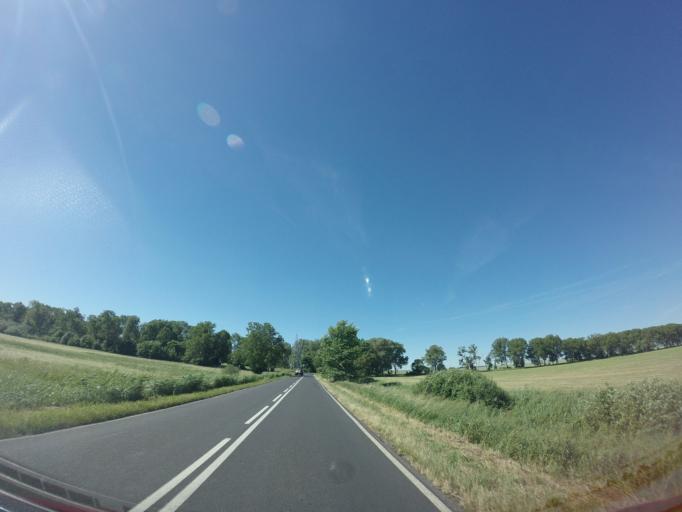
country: PL
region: West Pomeranian Voivodeship
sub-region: Powiat pyrzycki
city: Przelewice
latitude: 53.1533
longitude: 15.0346
